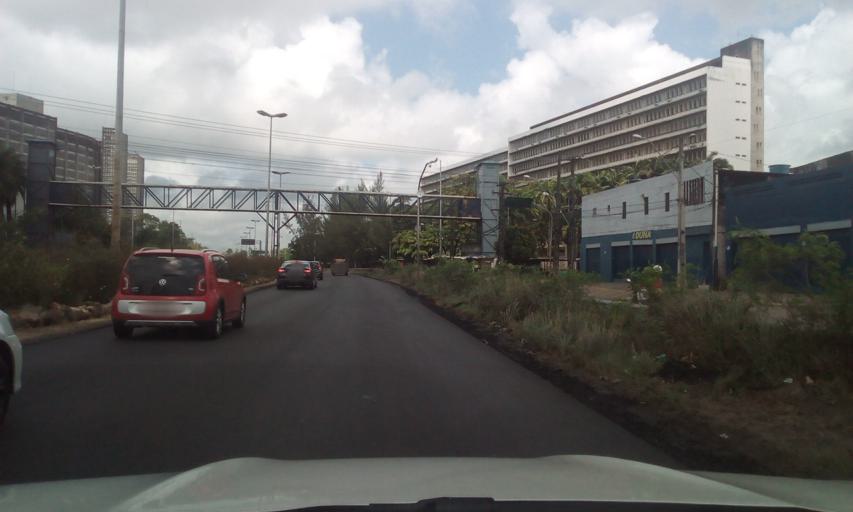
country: BR
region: Pernambuco
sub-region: Recife
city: Recife
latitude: -8.0460
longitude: -34.9448
